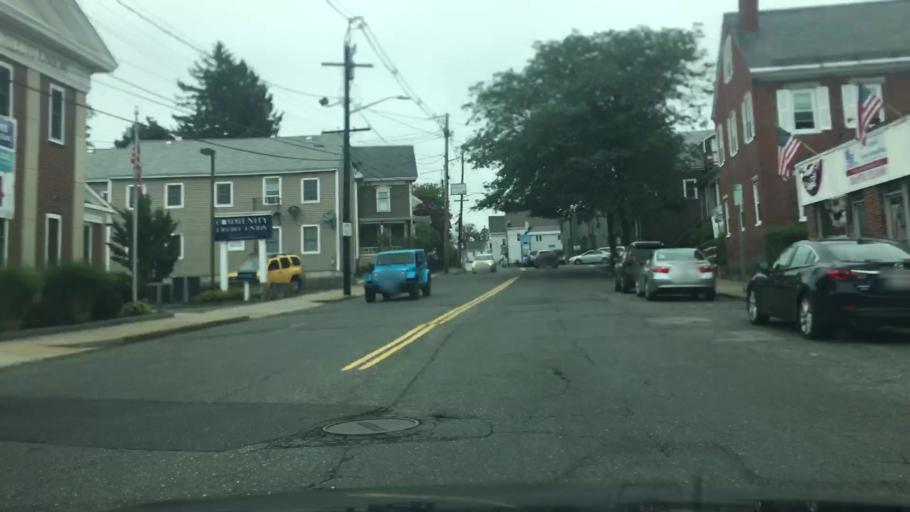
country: US
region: Massachusetts
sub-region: Essex County
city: Peabody
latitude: 42.5282
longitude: -70.9273
